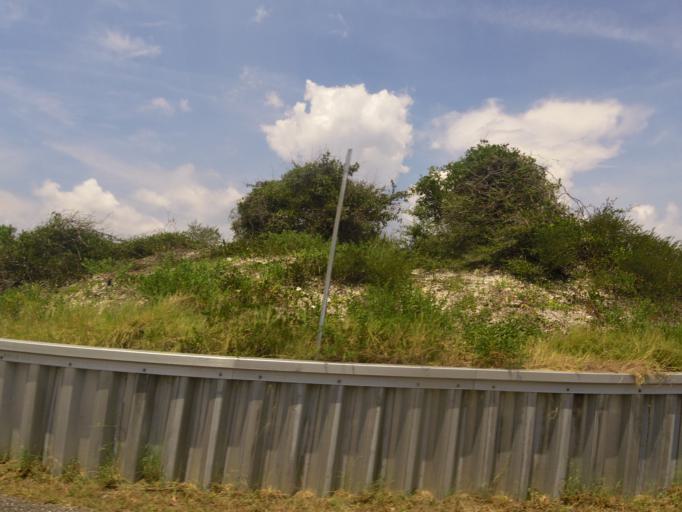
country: US
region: Florida
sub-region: Duval County
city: Atlantic Beach
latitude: 30.4444
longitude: -81.4146
